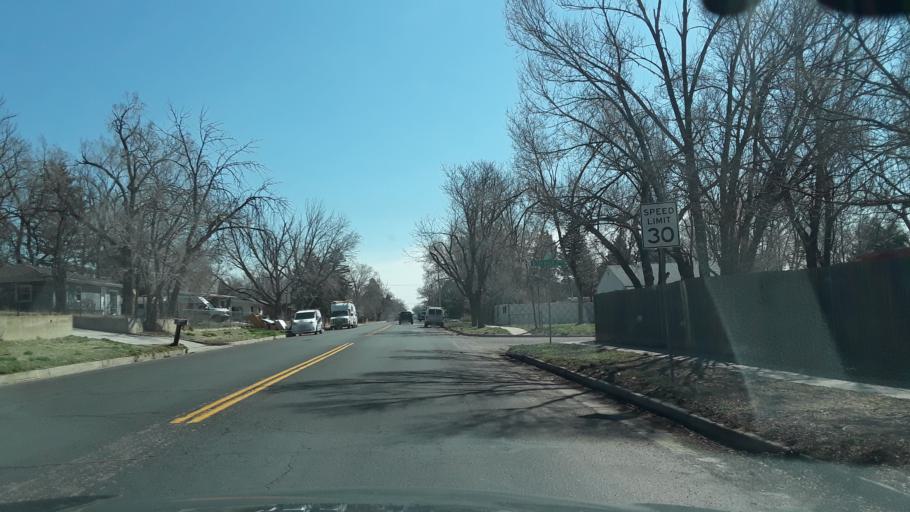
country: US
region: Colorado
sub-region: El Paso County
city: Colorado Springs
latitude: 38.8489
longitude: -104.7833
